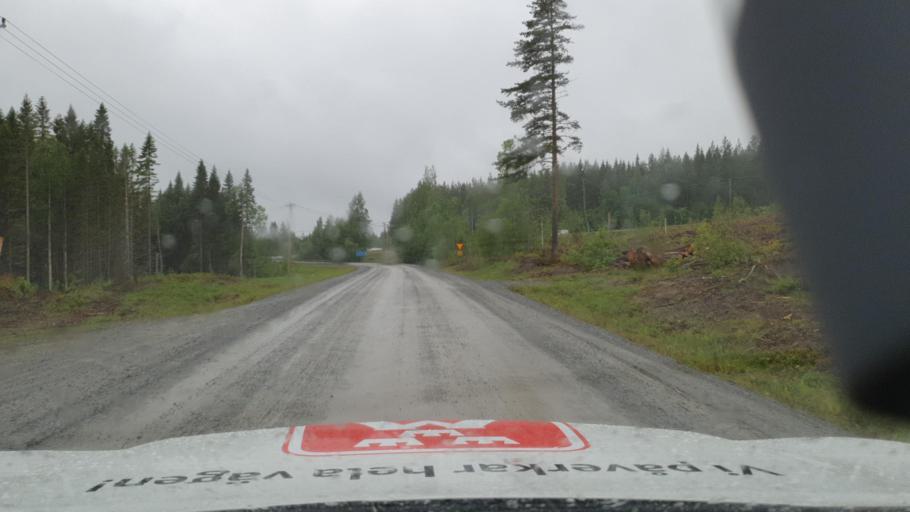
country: SE
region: Vaesterbotten
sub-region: Bjurholms Kommun
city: Bjurholm
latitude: 63.9304
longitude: 19.3588
